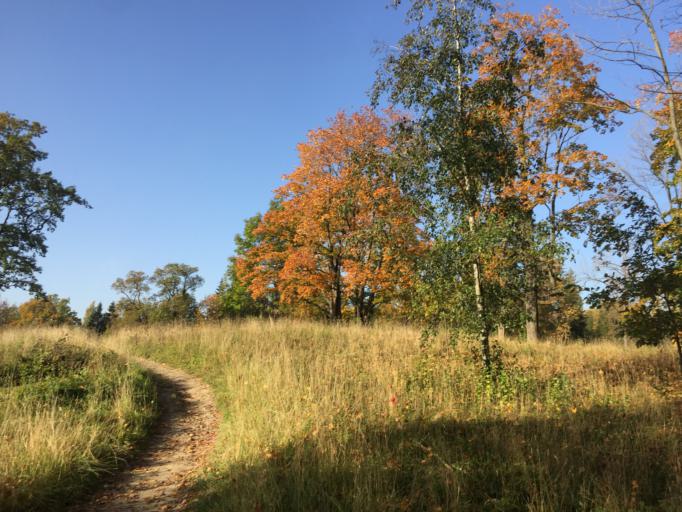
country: RU
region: St.-Petersburg
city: Pushkin
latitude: 59.7147
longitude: 30.3793
